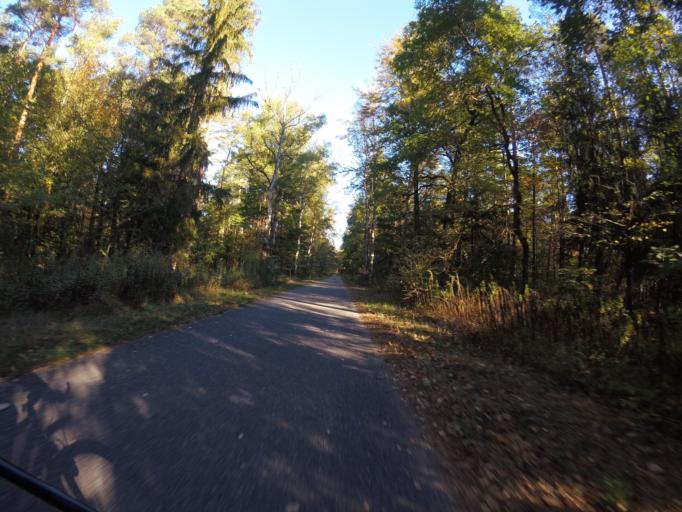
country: DE
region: Baden-Wuerttemberg
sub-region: Karlsruhe Region
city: Eggenstein-Leopoldshafen
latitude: 49.0523
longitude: 8.4085
